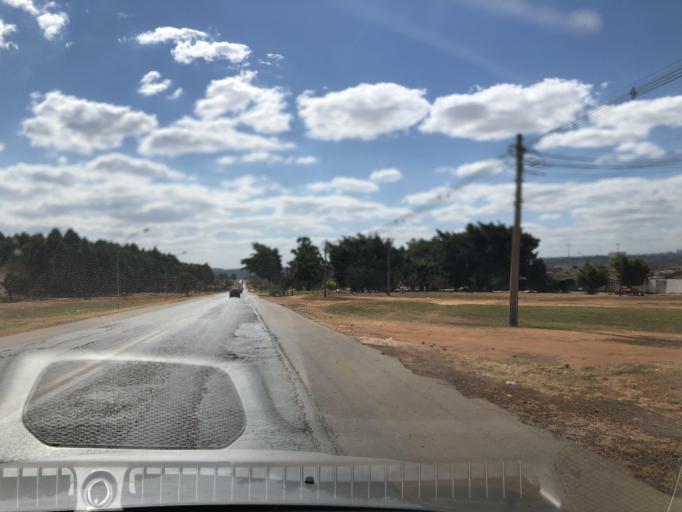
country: BR
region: Federal District
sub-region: Brasilia
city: Brasilia
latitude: -15.8932
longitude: -48.1495
